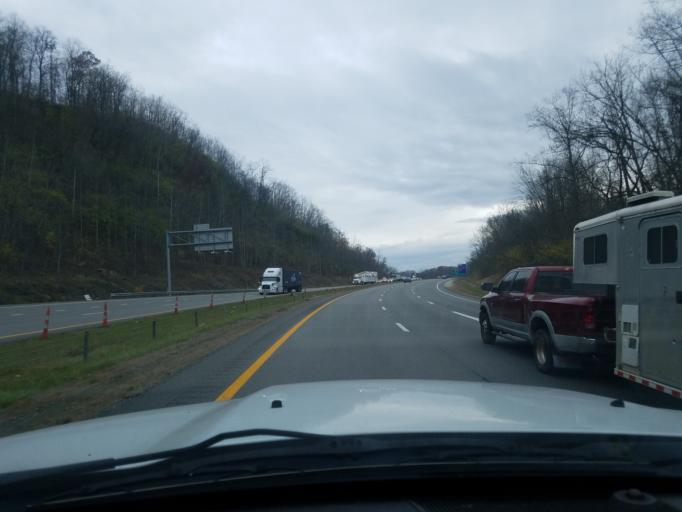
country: US
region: West Virginia
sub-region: Cabell County
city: Huntington
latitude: 38.3943
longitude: -82.4574
